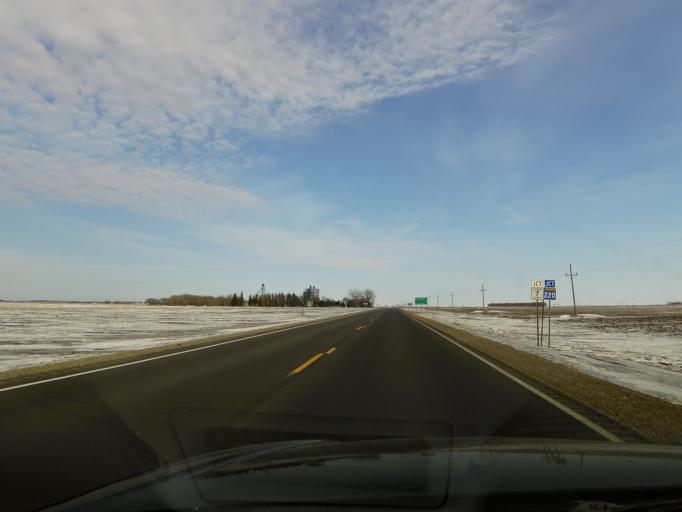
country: US
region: Minnesota
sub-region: Kittson County
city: Hallock
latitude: 48.5730
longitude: -97.1132
